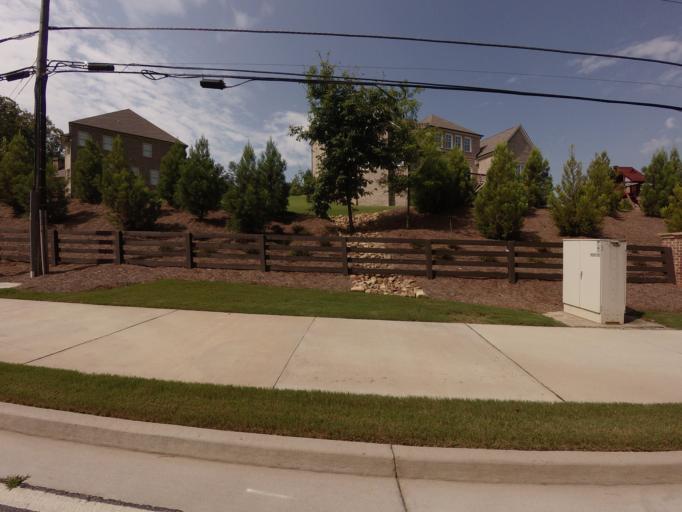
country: US
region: Georgia
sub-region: Fulton County
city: Johns Creek
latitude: 34.0301
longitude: -84.2306
